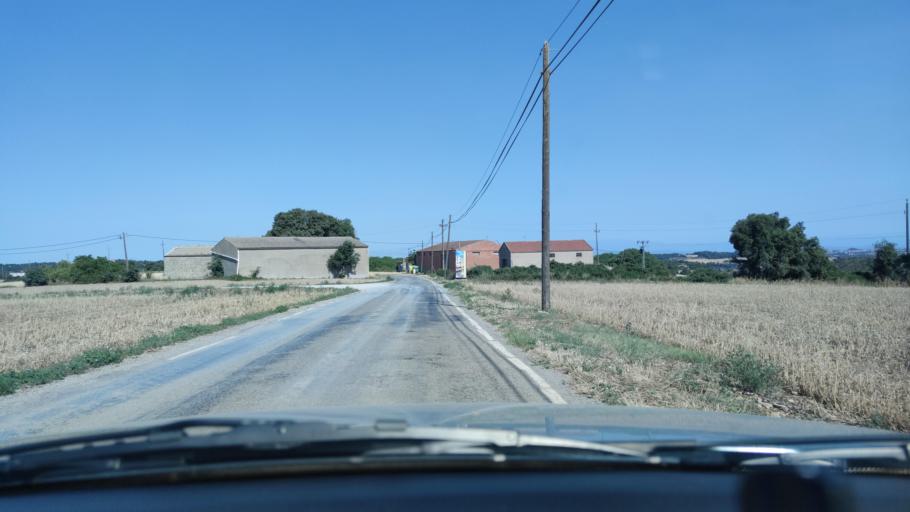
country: ES
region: Catalonia
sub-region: Provincia de Lleida
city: Sant Guim de Freixenet
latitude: 41.6459
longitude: 1.4066
